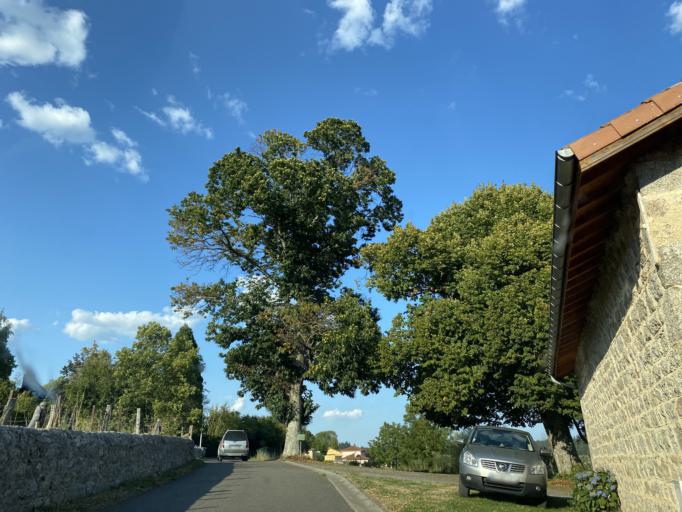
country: FR
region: Rhone-Alpes
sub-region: Departement de la Loire
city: Noiretable
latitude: 45.8131
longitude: 3.7568
